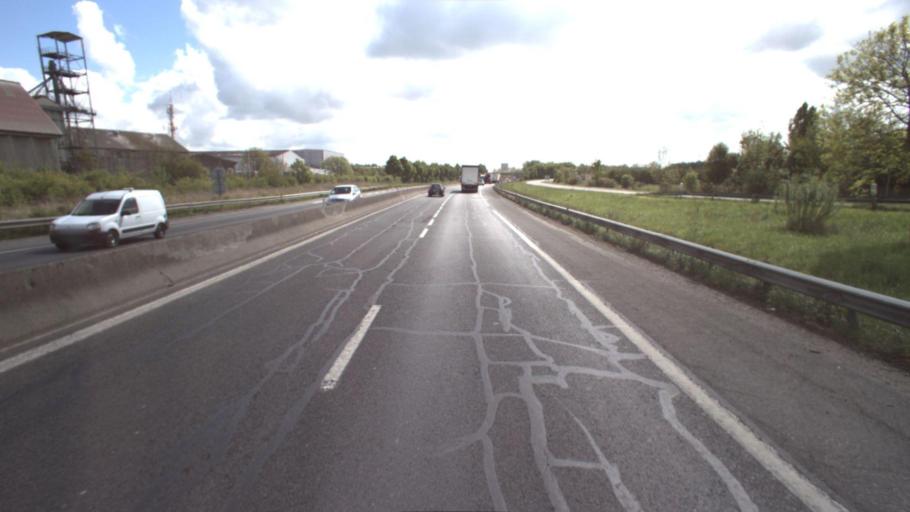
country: FR
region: Ile-de-France
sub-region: Departement de Seine-et-Marne
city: Tournan-en-Brie
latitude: 48.7358
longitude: 2.7710
